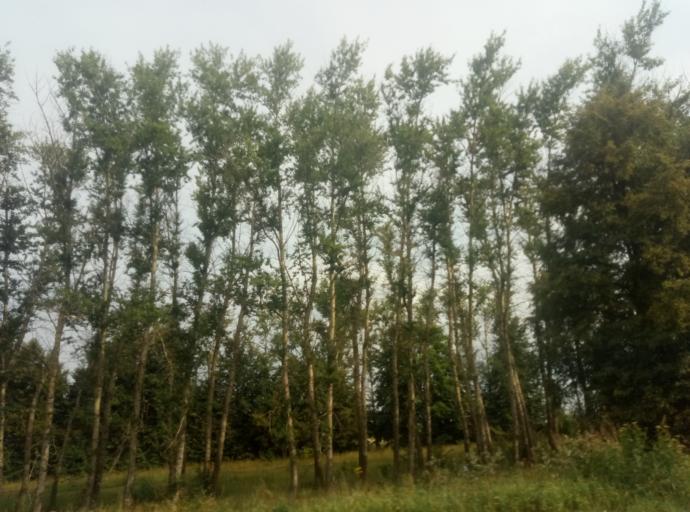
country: RU
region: Tula
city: Dubovka
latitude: 53.9012
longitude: 38.0112
